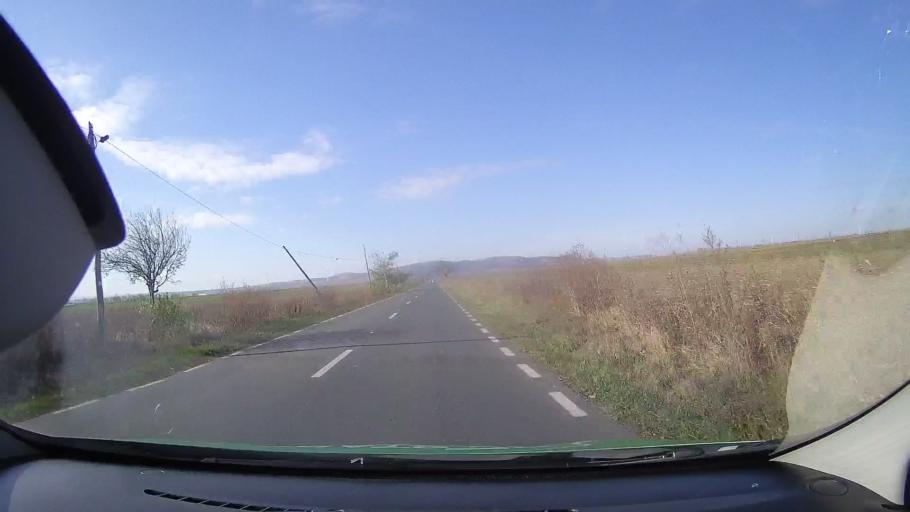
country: RO
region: Tulcea
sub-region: Comuna Valea Nucarilor
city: Valea Nucarilor
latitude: 45.0392
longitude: 28.9167
